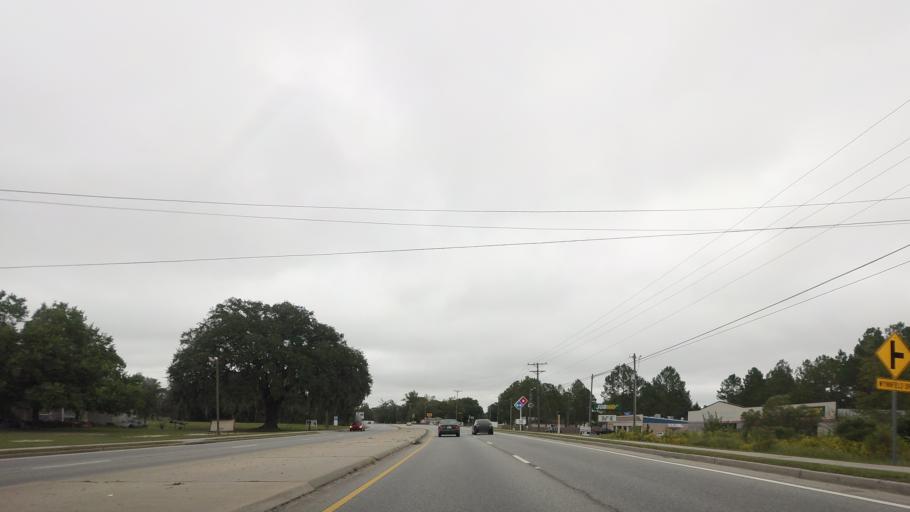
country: US
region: Georgia
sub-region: Lowndes County
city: Valdosta
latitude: 30.9284
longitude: -83.2452
